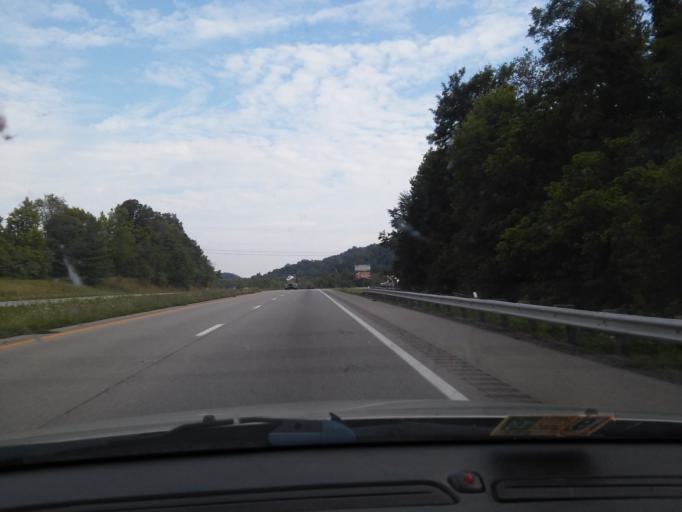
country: US
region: Ohio
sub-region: Jackson County
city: Jackson
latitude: 39.1700
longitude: -82.7446
